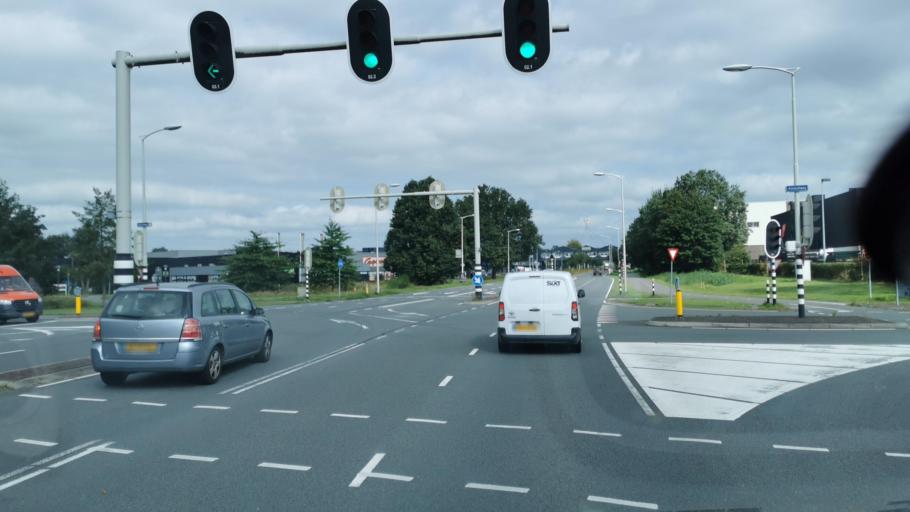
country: NL
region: Overijssel
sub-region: Gemeente Oldenzaal
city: Oldenzaal
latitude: 52.2937
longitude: 6.9246
